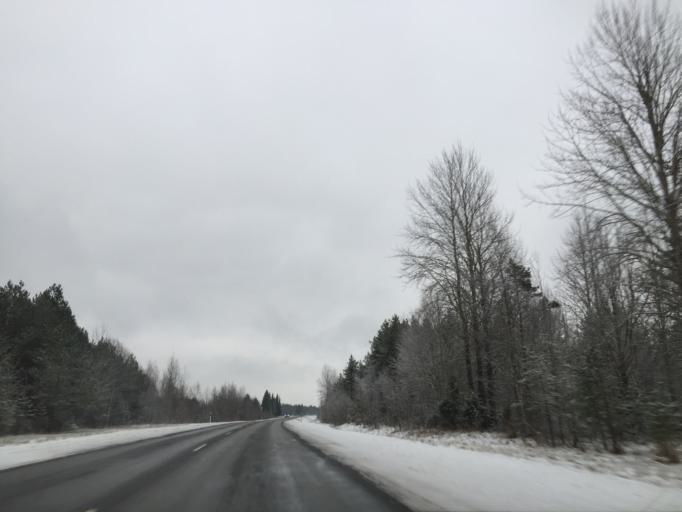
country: EE
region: Laeaene
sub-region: Lihula vald
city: Lihula
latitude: 58.6230
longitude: 23.8983
